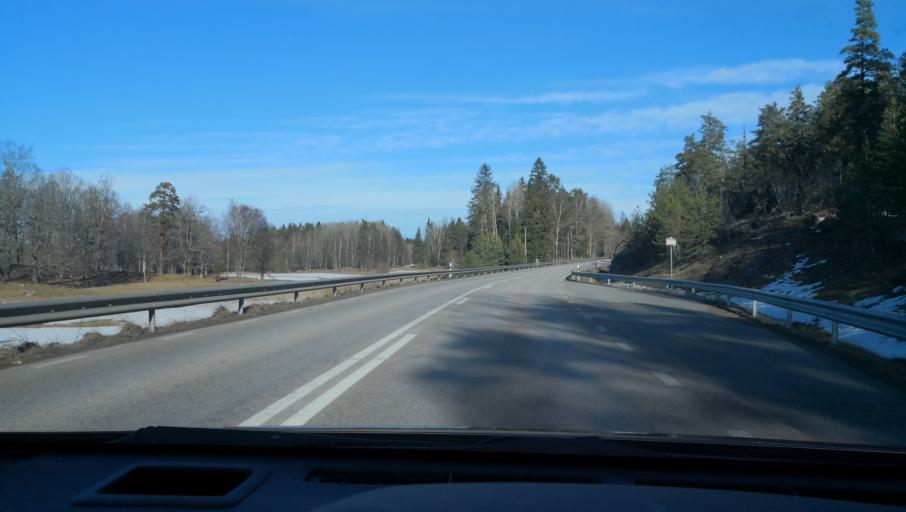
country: SE
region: Uppsala
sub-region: Osthammars Kommun
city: Osterbybruk
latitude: 60.1428
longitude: 17.8204
